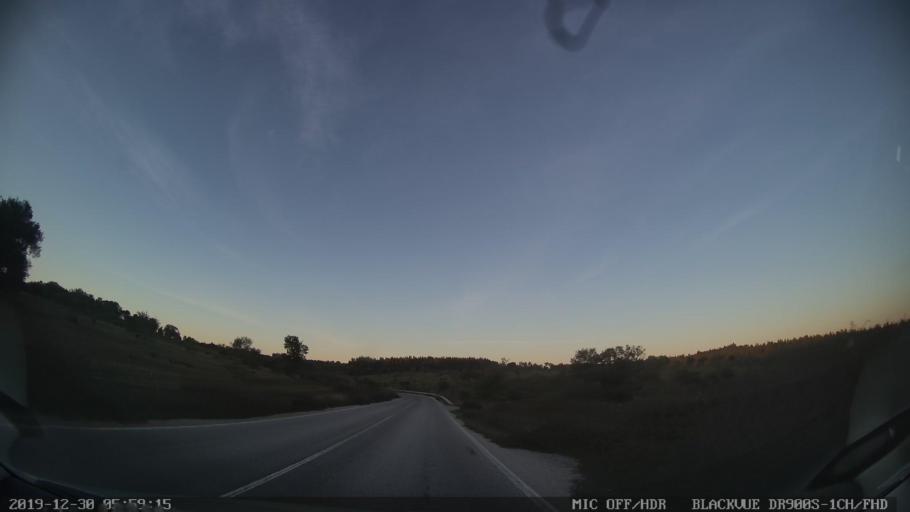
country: PT
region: Castelo Branco
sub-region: Idanha-A-Nova
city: Idanha-a-Nova
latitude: 40.0425
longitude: -7.2423
